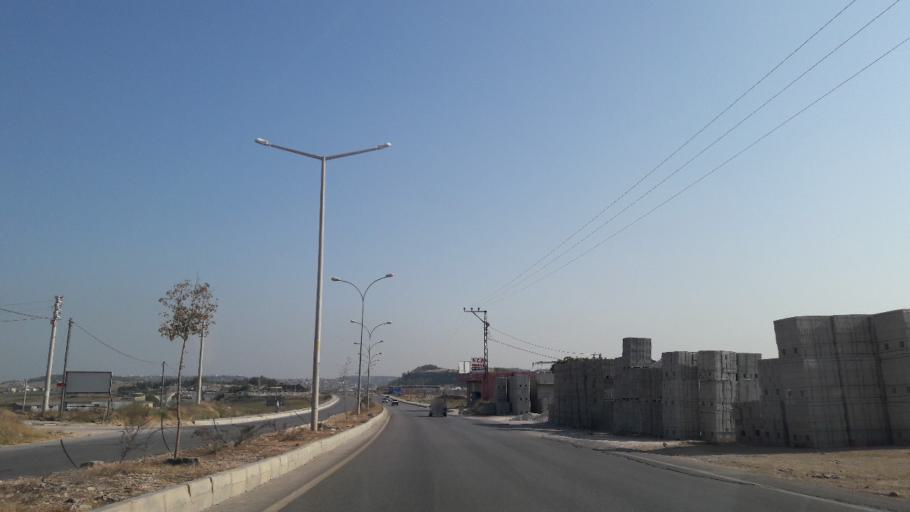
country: TR
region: Adana
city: Yuregir
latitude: 37.0475
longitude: 35.4369
